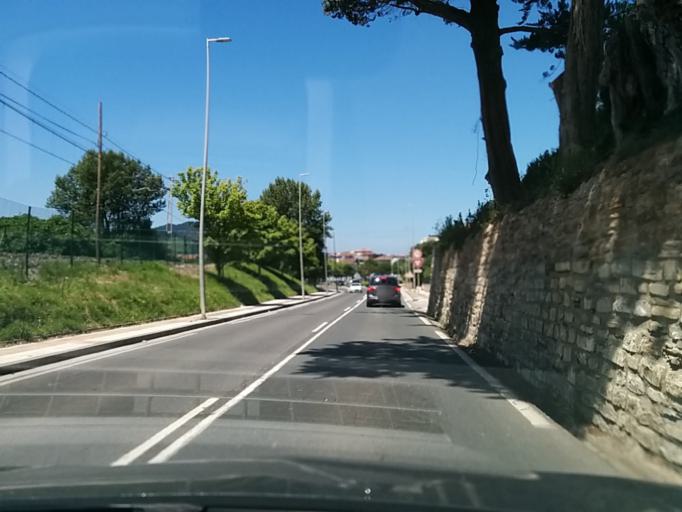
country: ES
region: Basque Country
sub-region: Provincia de Guipuzcoa
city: Zarautz
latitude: 43.2830
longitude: -2.1542
